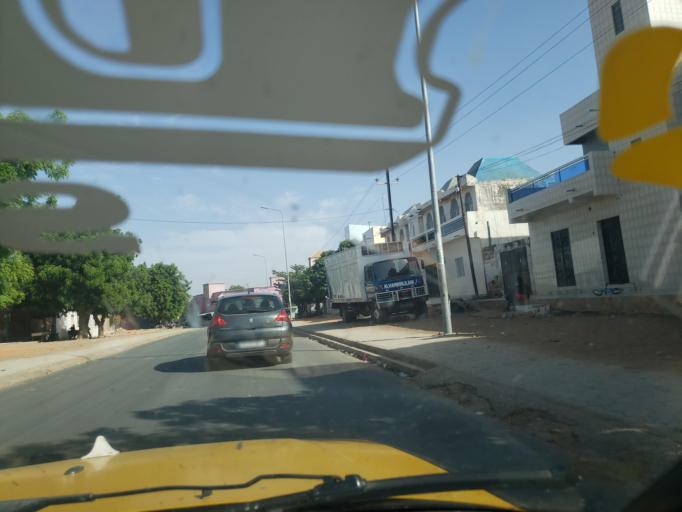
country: SN
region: Louga
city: Louga
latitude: 15.6221
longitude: -16.2114
